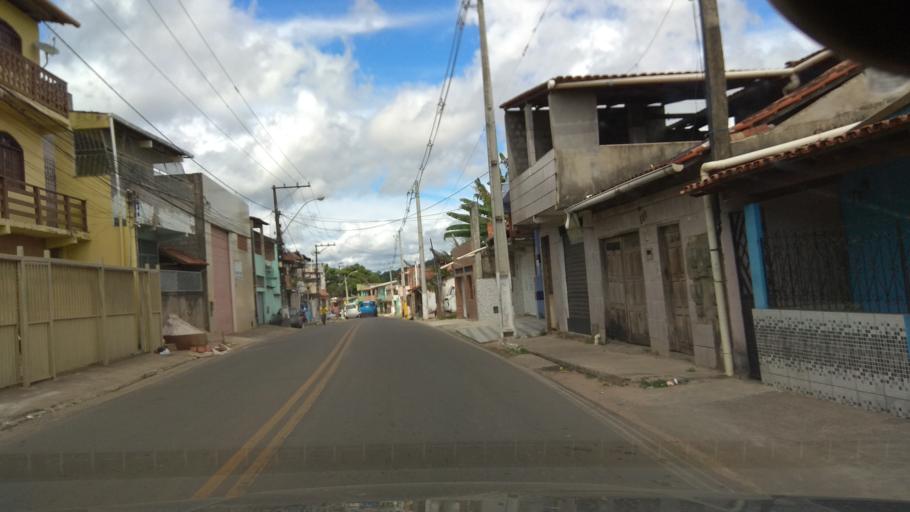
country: BR
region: Bahia
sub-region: Ilheus
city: Ilheus
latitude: -14.7854
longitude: -39.0601
